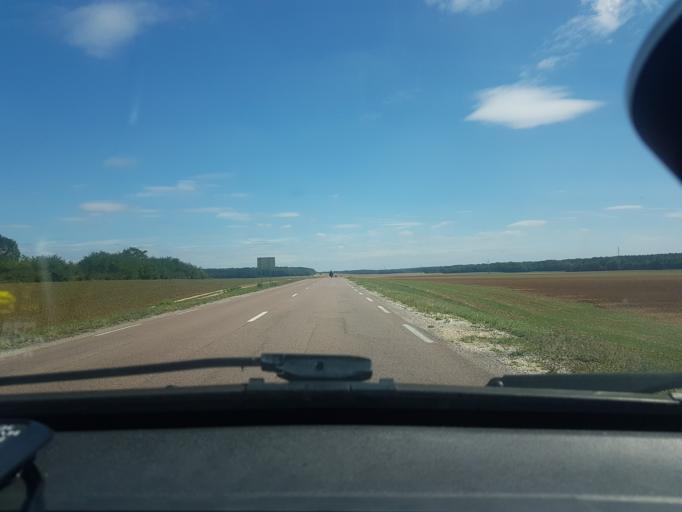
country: FR
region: Bourgogne
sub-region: Departement de la Cote-d'Or
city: Pontailler-sur-Saone
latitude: 47.3996
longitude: 5.4240
